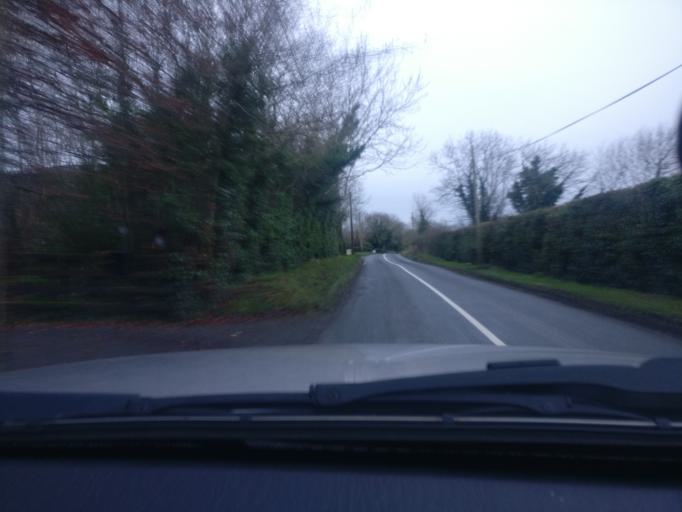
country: IE
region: Leinster
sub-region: Kildare
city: Kilcock
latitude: 53.4753
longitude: -6.6222
